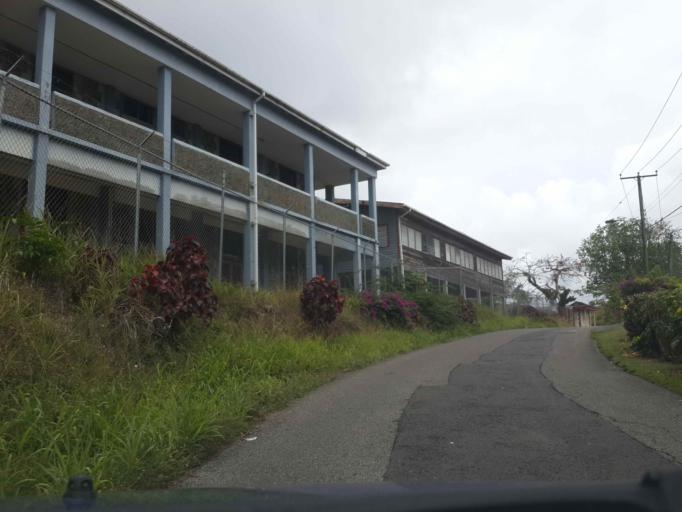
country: LC
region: Castries Quarter
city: Castries
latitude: 13.9968
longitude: -60.9943
